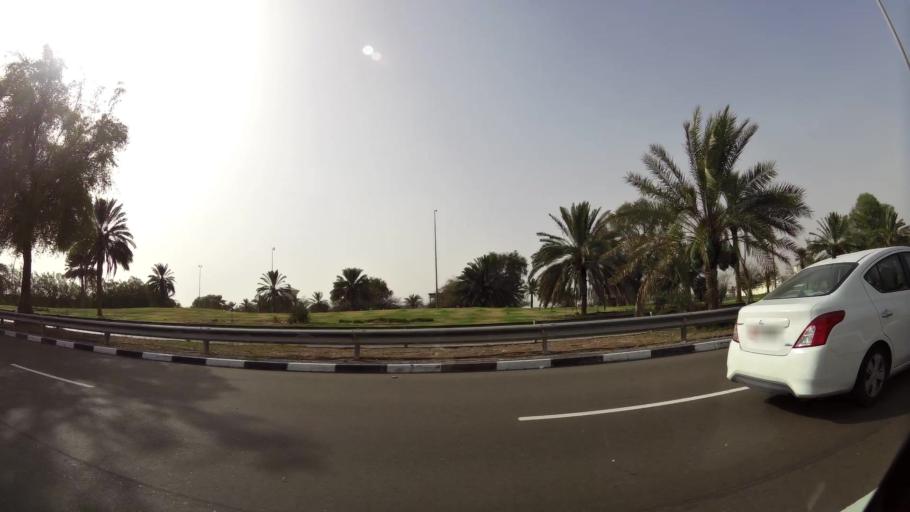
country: AE
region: Abu Dhabi
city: Al Ain
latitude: 24.1860
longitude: 55.6009
